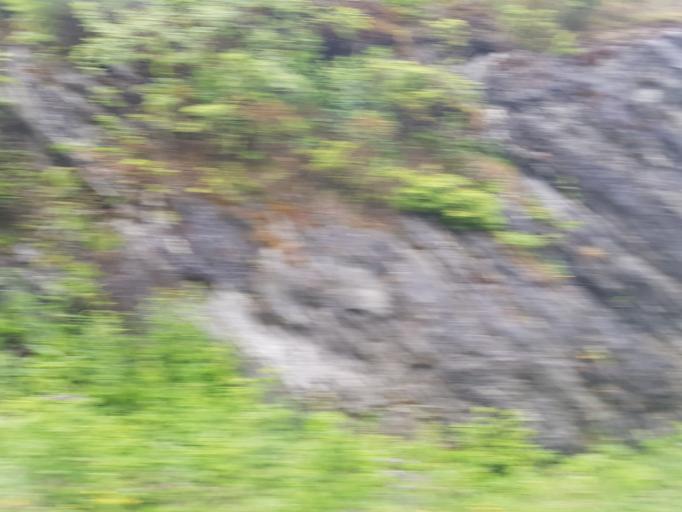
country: NO
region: Sor-Trondelag
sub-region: Selbu
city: Mebonden
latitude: 63.3083
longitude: 11.0794
